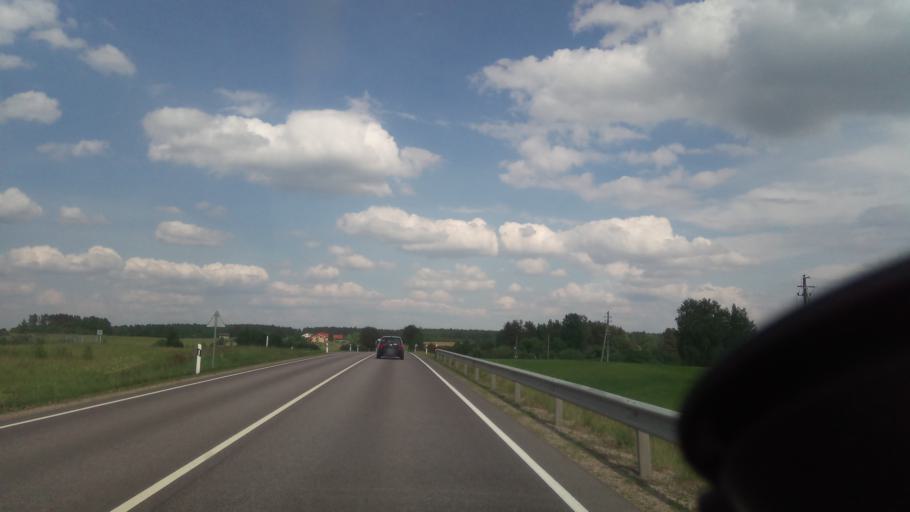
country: LT
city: Trakai
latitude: 54.6115
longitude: 24.8835
